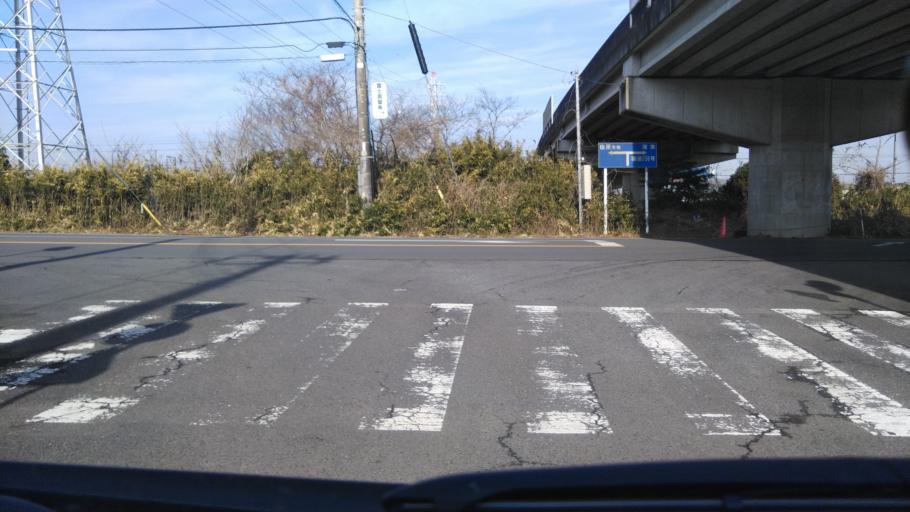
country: JP
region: Chiba
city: Katori-shi
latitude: 35.8958
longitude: 140.5201
